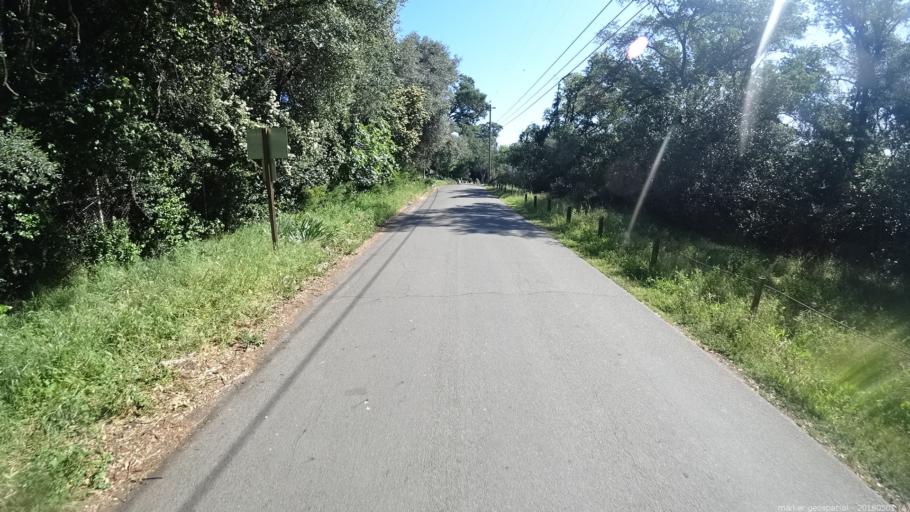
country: US
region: California
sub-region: Sacramento County
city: Arden-Arcade
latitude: 38.6421
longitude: -121.3775
